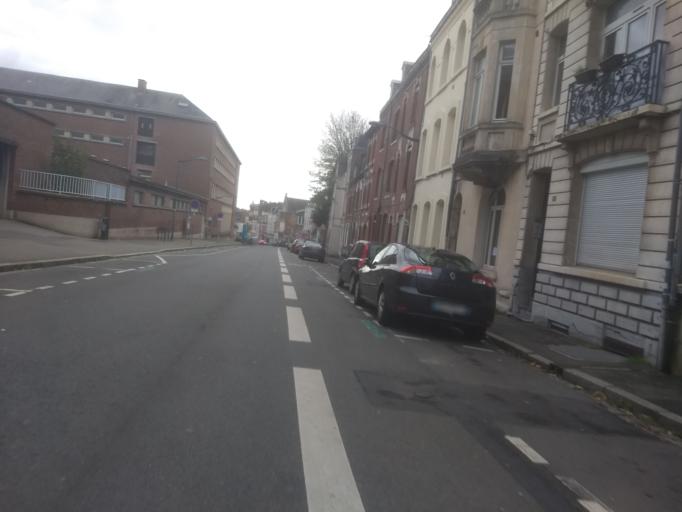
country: FR
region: Nord-Pas-de-Calais
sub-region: Departement du Pas-de-Calais
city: Sainte-Catherine
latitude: 50.2943
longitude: 2.7657
